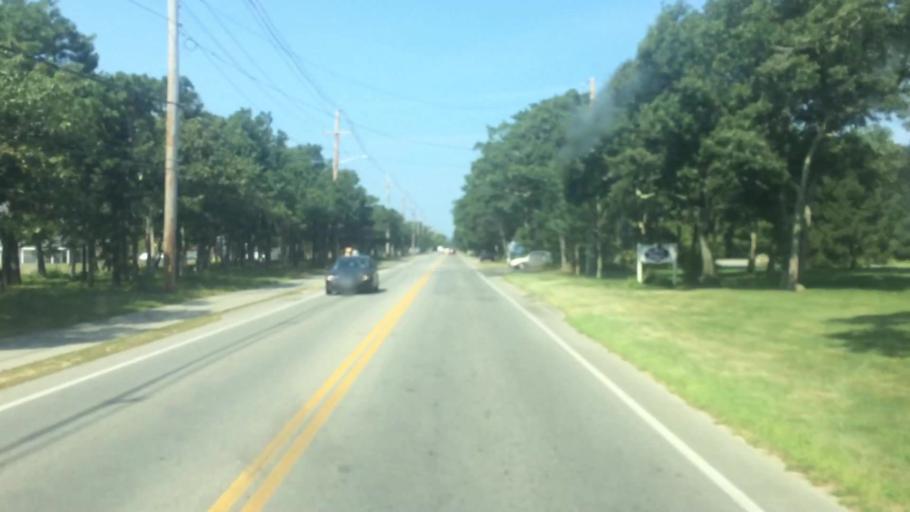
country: US
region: Massachusetts
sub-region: Dukes County
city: Vineyard Haven
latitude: 41.4182
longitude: -70.5919
